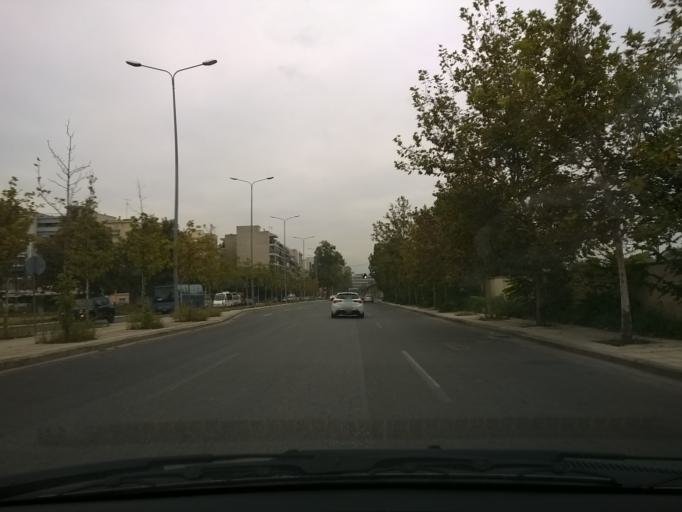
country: GR
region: Central Macedonia
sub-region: Nomos Thessalonikis
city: Thessaloniki
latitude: 40.6416
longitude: 22.9257
